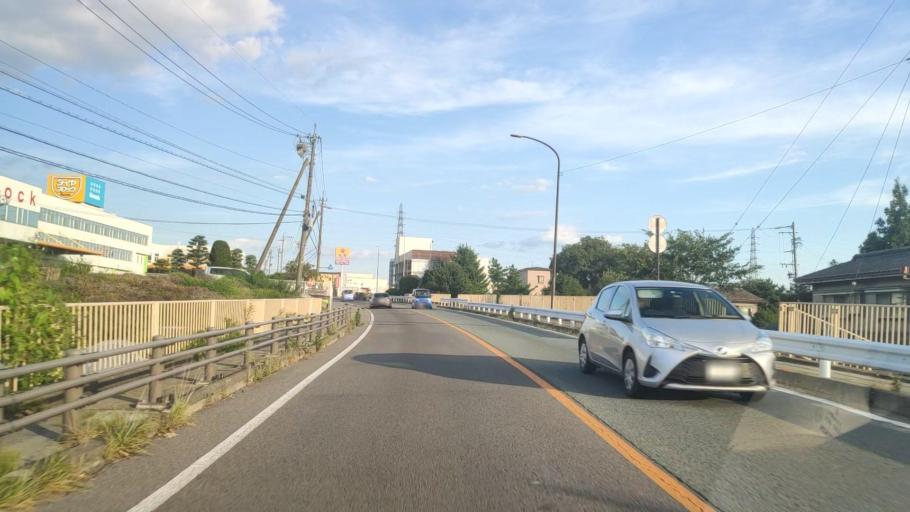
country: JP
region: Nagano
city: Kamimaruko
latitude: 36.3529
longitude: 138.3500
